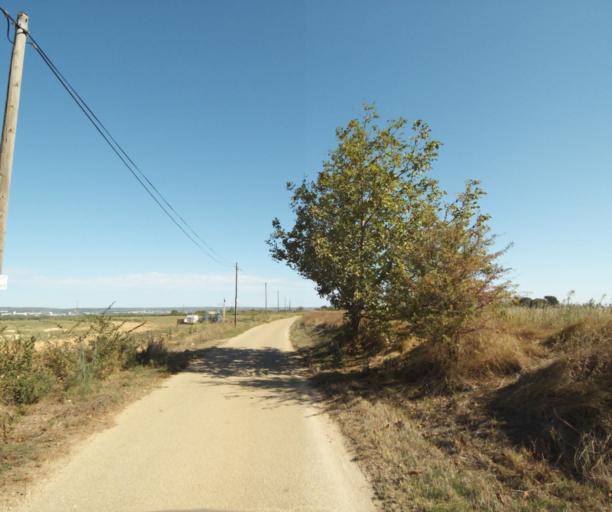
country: FR
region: Languedoc-Roussillon
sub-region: Departement du Gard
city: Bouillargues
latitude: 43.7914
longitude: 4.4176
